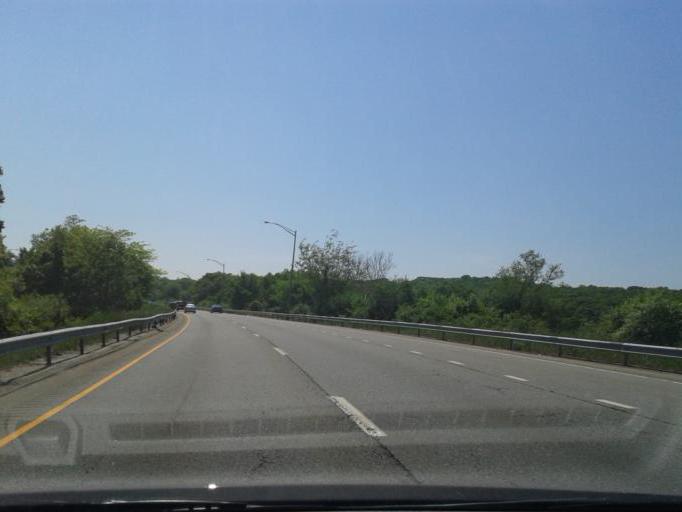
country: US
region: Connecticut
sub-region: New London County
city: Old Mystic
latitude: 41.3754
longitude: -71.9598
